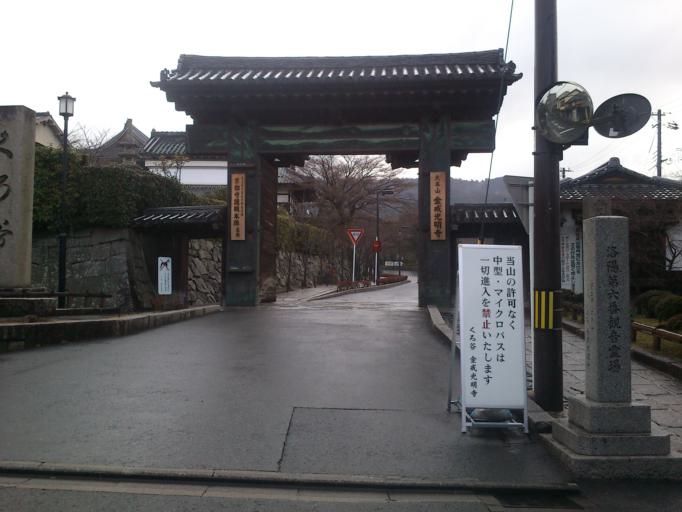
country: JP
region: Kyoto
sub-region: Kyoto-shi
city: Kamigyo-ku
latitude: 35.0183
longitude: 135.7858
